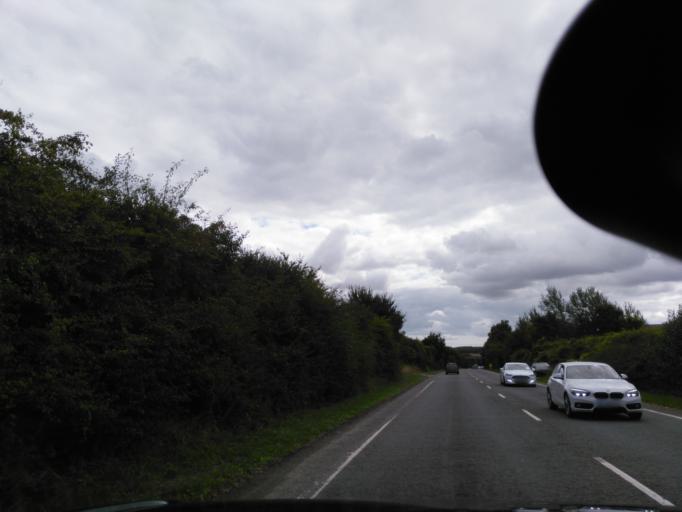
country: GB
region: England
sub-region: Dorset
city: Blandford Forum
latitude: 50.8725
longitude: -2.1557
